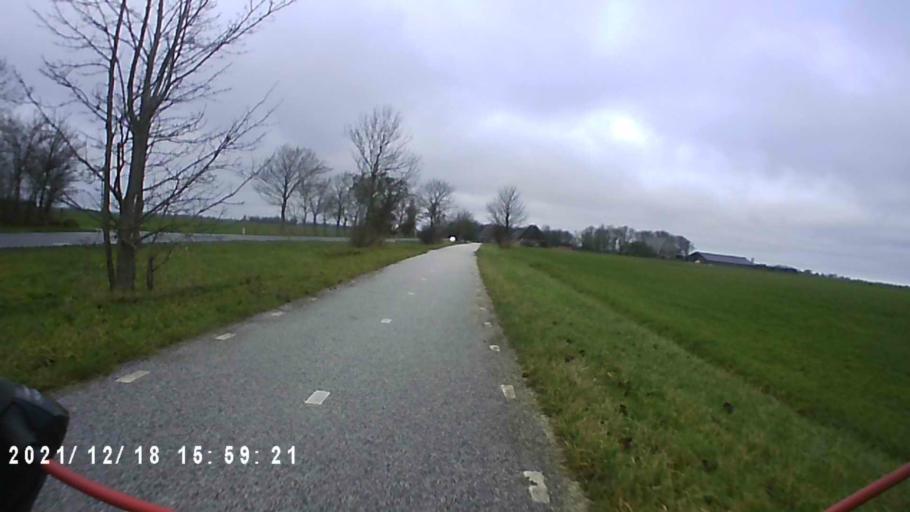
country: NL
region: Friesland
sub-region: Gemeente Dongeradeel
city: Anjum
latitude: 53.3393
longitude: 6.0904
